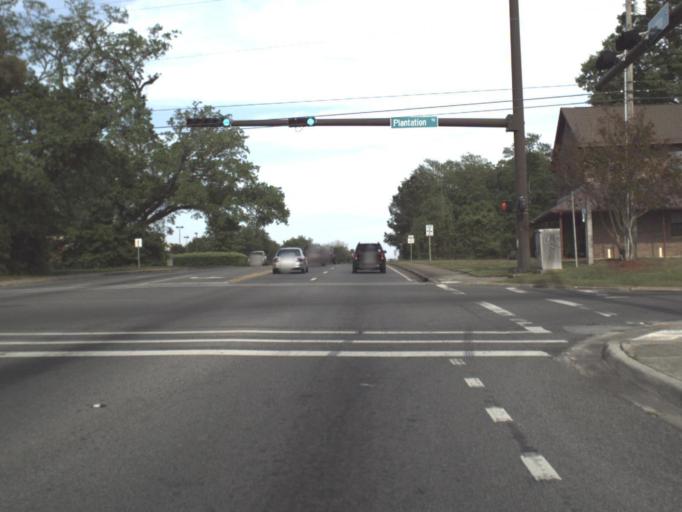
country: US
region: Florida
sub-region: Escambia County
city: Ferry Pass
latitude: 30.4959
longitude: -87.2281
